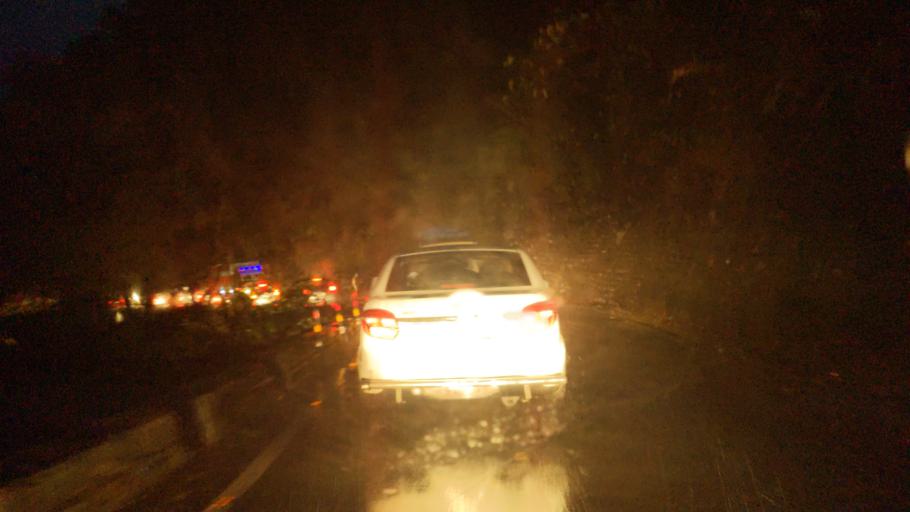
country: IN
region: Uttarakhand
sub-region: Naini Tal
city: Haldwani
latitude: 29.2790
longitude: 79.5449
